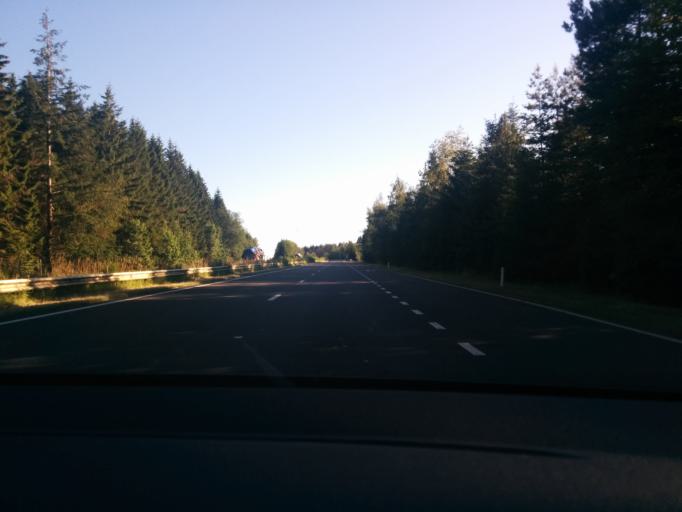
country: BE
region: Wallonia
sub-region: Province du Luxembourg
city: Saint-Hubert
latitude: 50.0527
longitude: 5.4006
